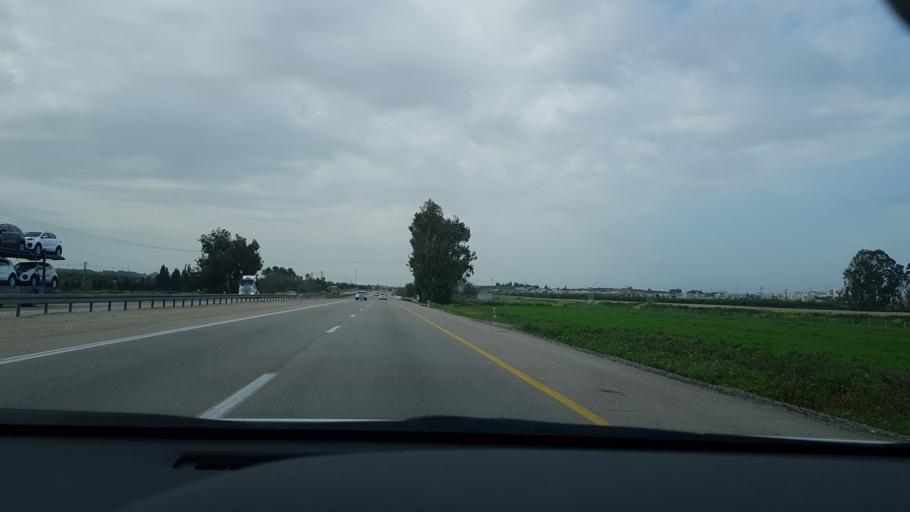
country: IL
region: Southern District
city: Ashqelon
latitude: 31.7066
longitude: 34.6230
